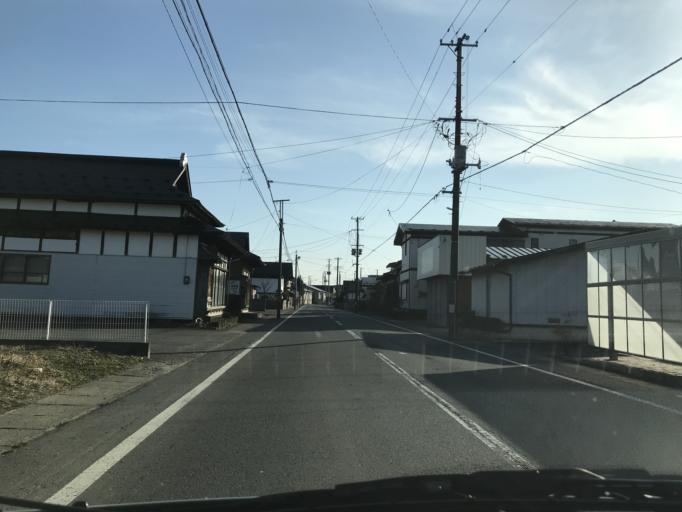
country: JP
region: Iwate
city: Kitakami
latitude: 39.2603
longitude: 141.1138
